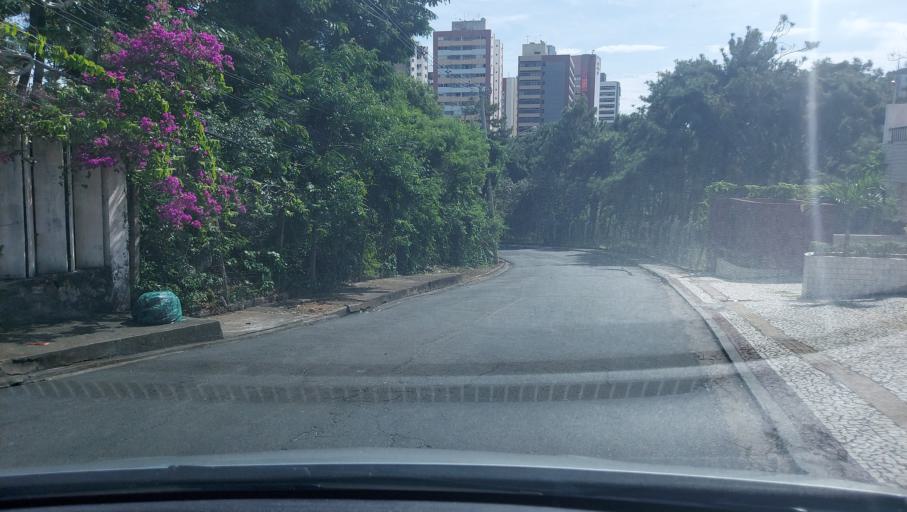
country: BR
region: Bahia
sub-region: Salvador
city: Salvador
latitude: -12.9829
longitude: -38.4484
